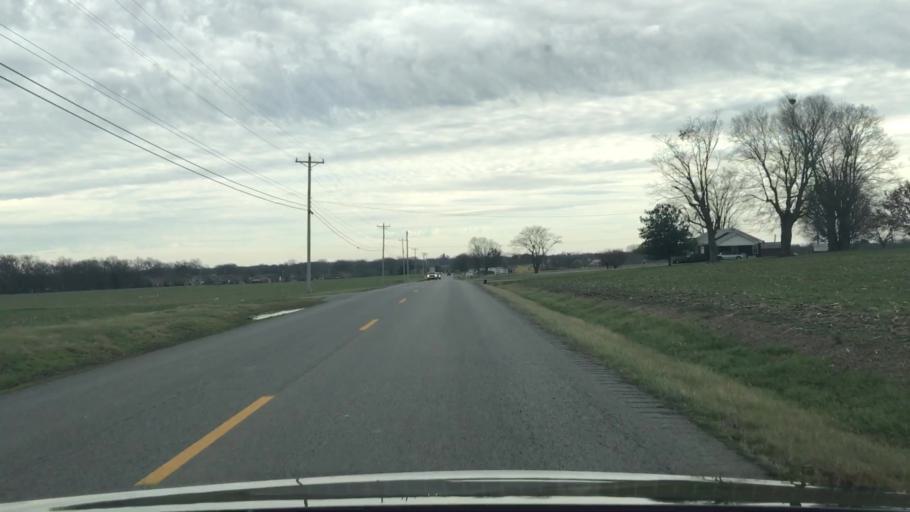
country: US
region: Kentucky
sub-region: Christian County
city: Hopkinsville
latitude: 36.8616
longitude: -87.5336
